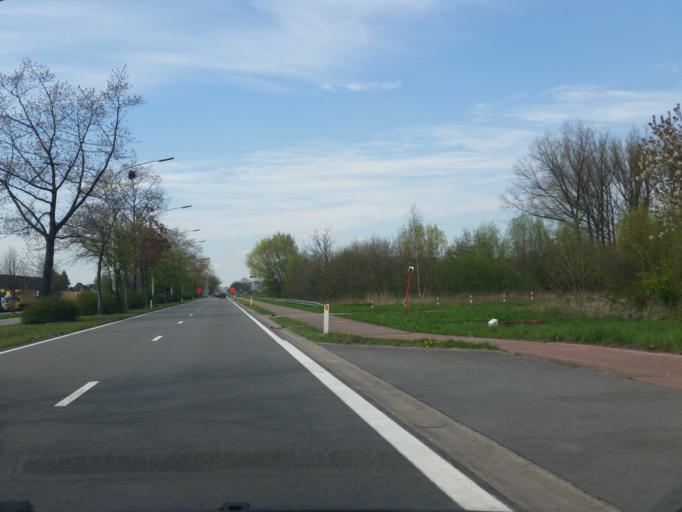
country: BE
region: Flanders
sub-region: Provincie Antwerpen
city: Bornem
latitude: 51.0968
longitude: 4.2573
